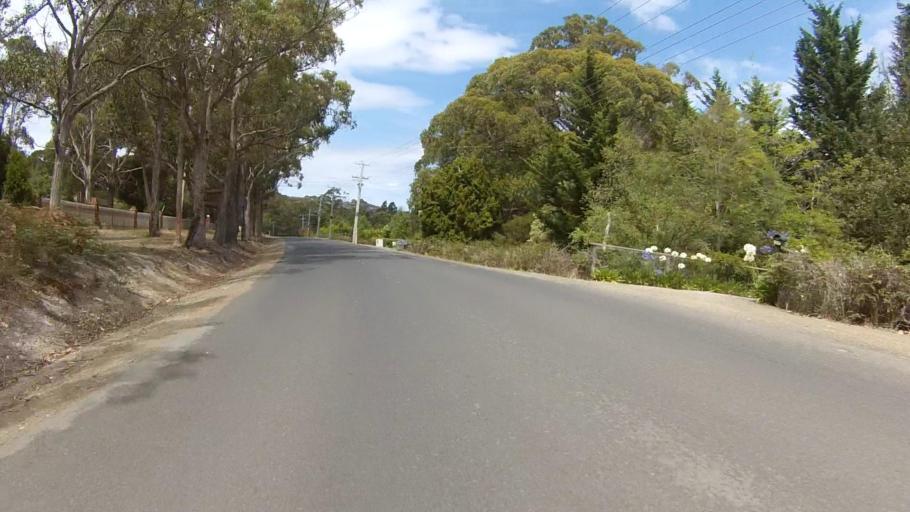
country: AU
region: Tasmania
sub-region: Kingborough
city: Blackmans Bay
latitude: -43.0126
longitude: 147.2885
